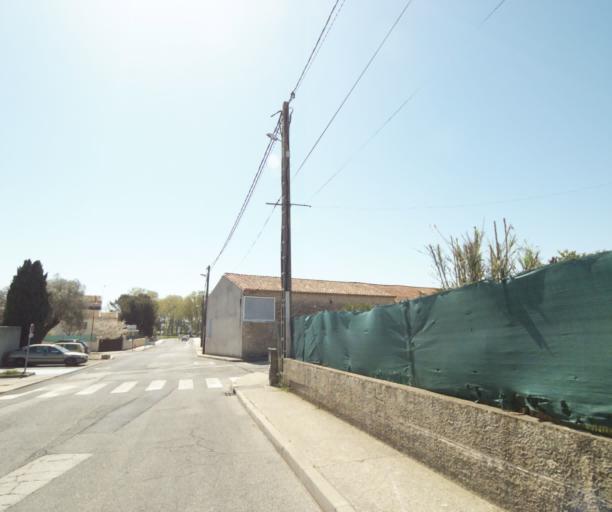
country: FR
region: Languedoc-Roussillon
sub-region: Departement de l'Herault
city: Baillargues
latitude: 43.6583
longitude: 4.0080
